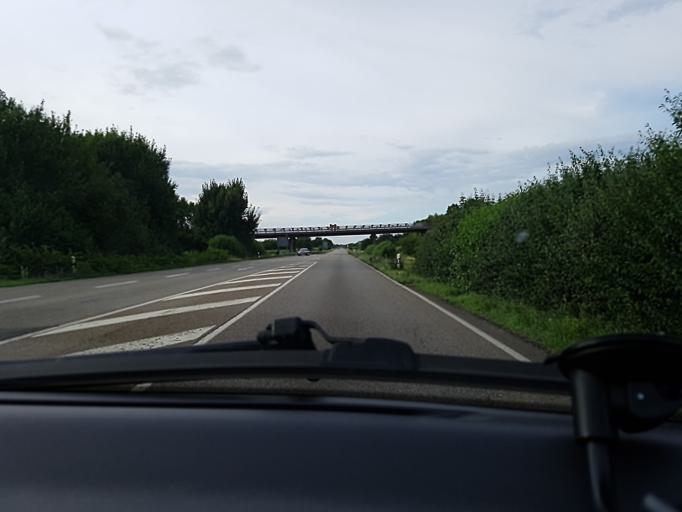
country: DE
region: Baden-Wuerttemberg
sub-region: Freiburg Region
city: Offenburg
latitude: 48.5026
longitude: 7.9574
